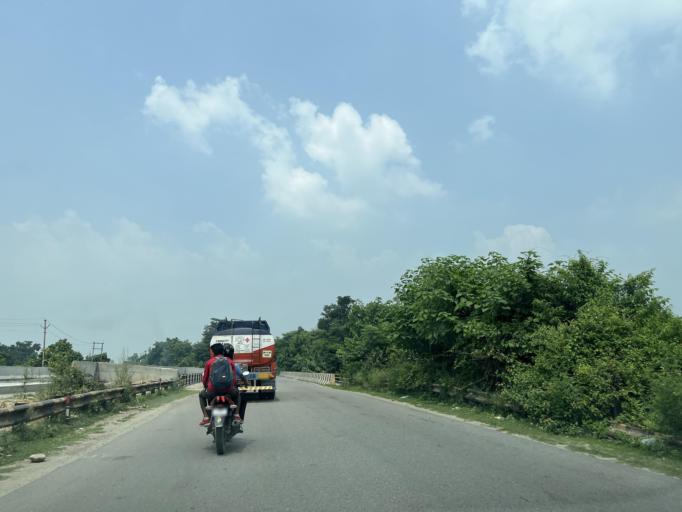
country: IN
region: Uttarakhand
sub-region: Haridwar
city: Haridwar
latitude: 29.8554
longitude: 78.1866
